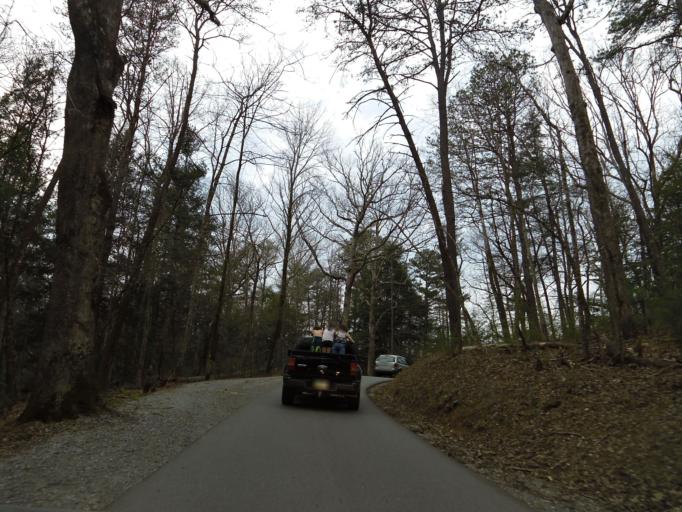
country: US
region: Tennessee
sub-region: Blount County
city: Wildwood
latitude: 35.6068
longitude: -83.8065
